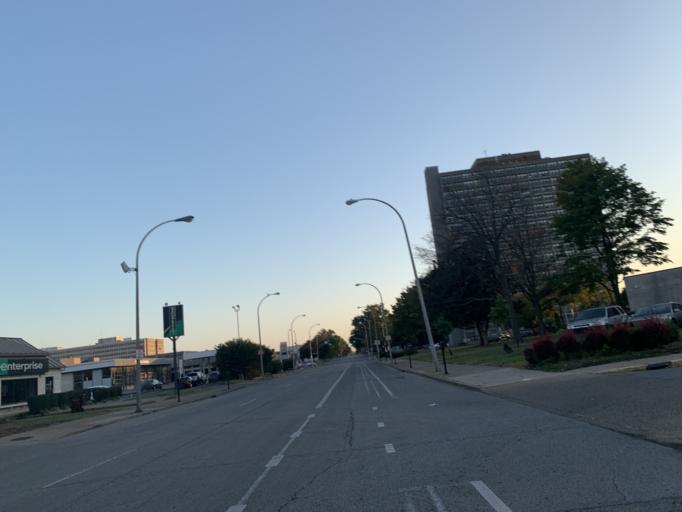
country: US
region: Kentucky
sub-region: Jefferson County
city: Louisville
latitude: 38.2531
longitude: -85.7640
